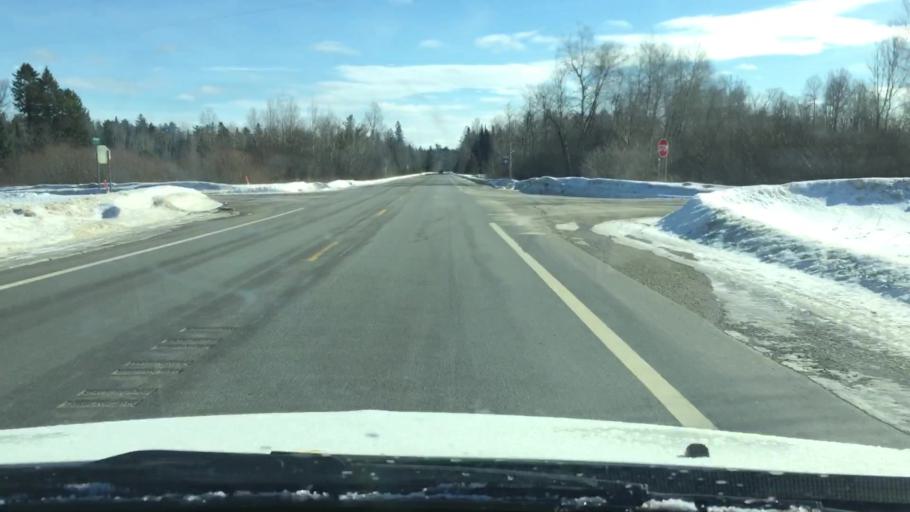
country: US
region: Michigan
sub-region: Charlevoix County
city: East Jordan
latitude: 45.0606
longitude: -85.0781
